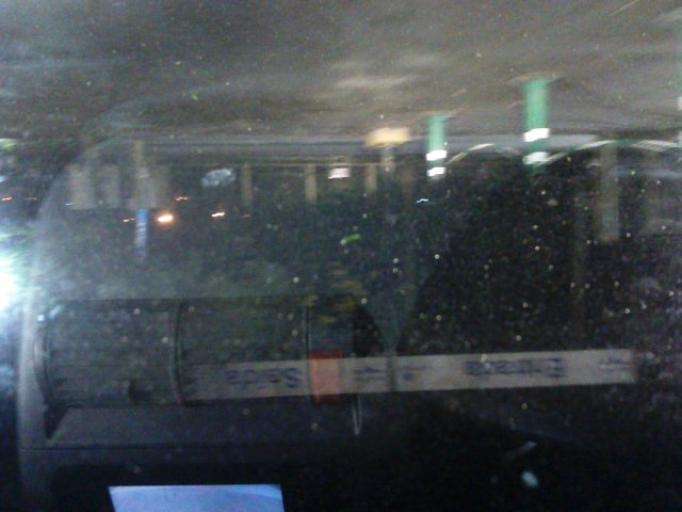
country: BR
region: Sao Paulo
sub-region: Sao Jose Dos Campos
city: Sao Jose dos Campos
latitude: -23.1984
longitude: -45.9168
